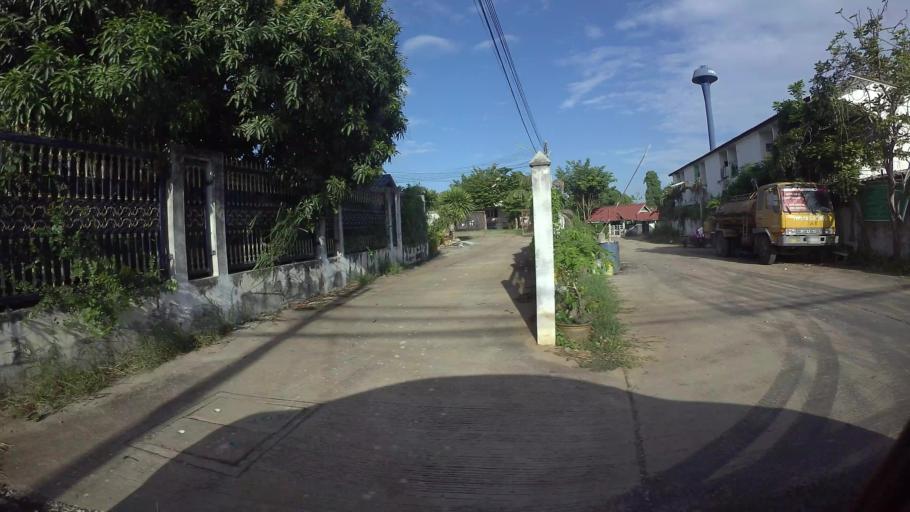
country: TH
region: Chon Buri
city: Sattahip
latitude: 12.6709
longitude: 100.9157
